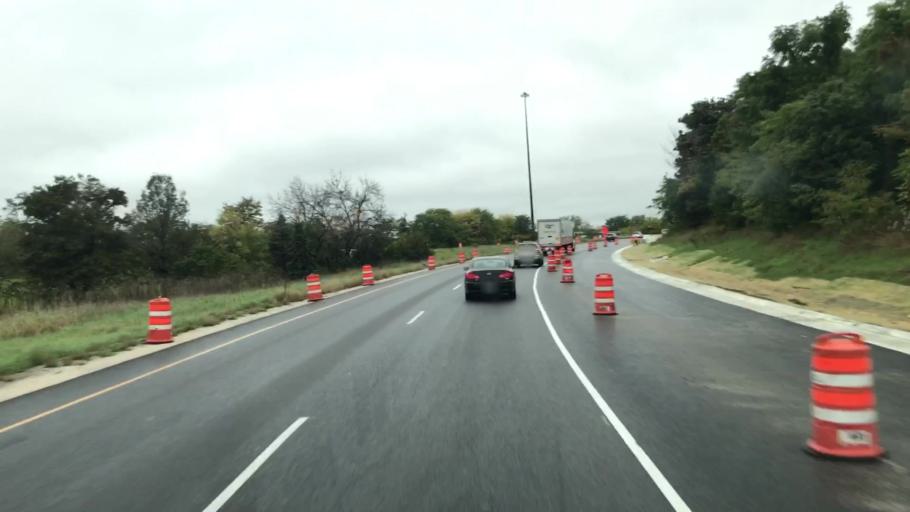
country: US
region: Wisconsin
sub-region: Milwaukee County
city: Greenfield
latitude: 42.9640
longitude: -88.0364
